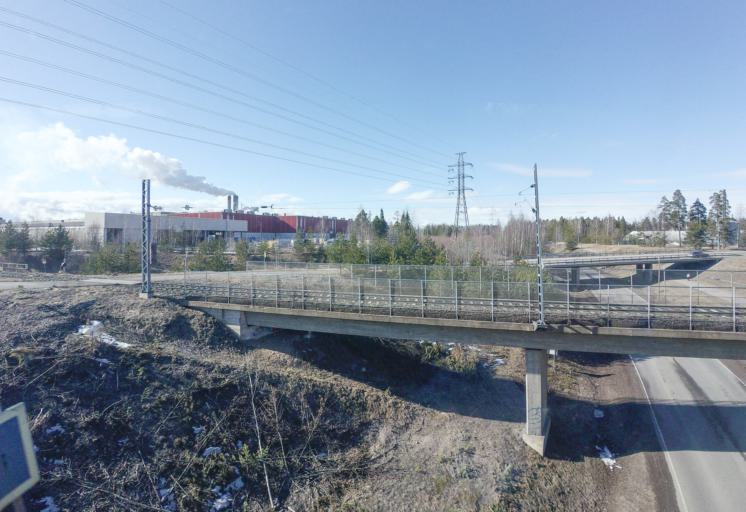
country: FI
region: South Karelia
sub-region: Lappeenranta
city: Lappeenranta
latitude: 61.0639
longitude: 28.2565
